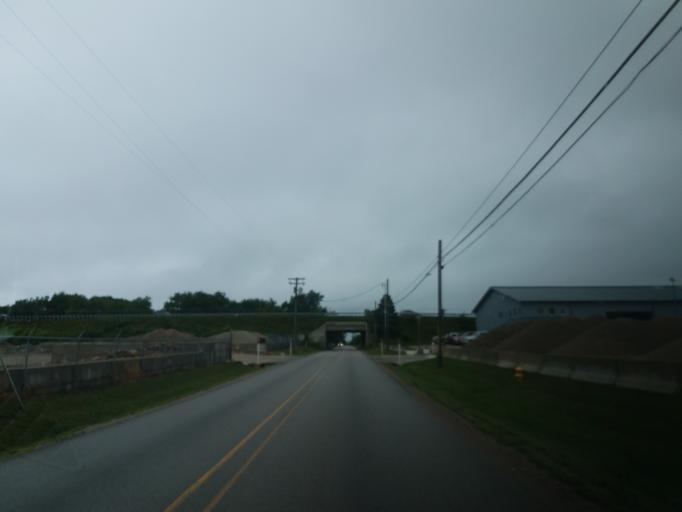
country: US
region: Illinois
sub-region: McLean County
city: Bloomington
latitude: 40.4583
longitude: -88.9815
